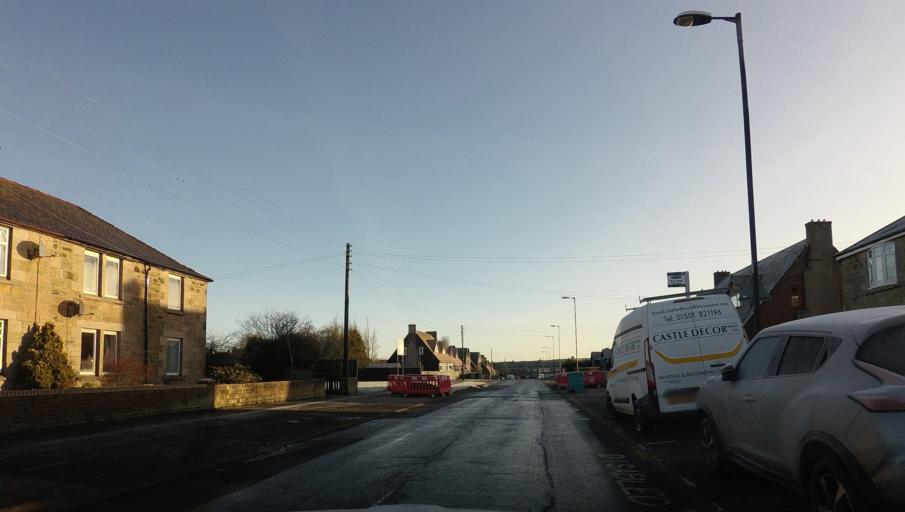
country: GB
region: Scotland
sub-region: North Lanarkshire
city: Shotts
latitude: 55.8222
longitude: -3.8014
